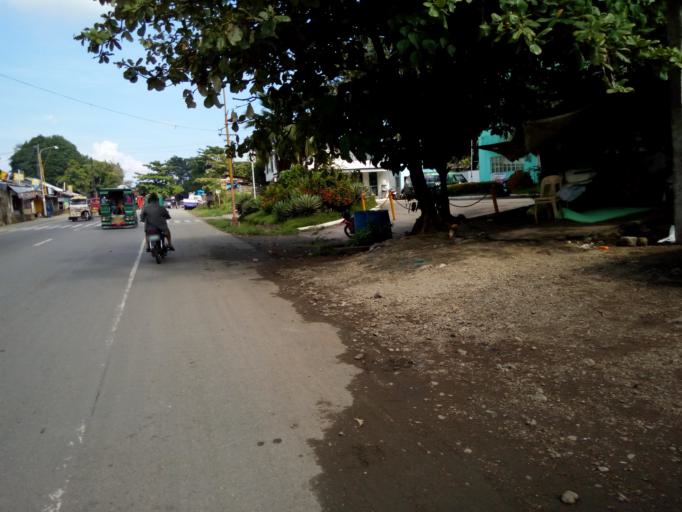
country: PH
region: Caraga
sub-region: Province of Surigao del Norte
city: Surigao
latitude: 9.7766
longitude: 125.4825
